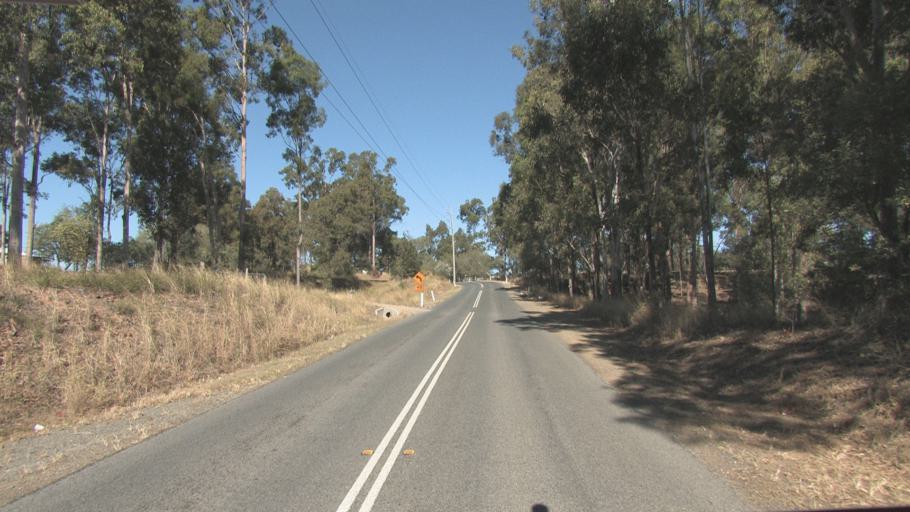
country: AU
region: Queensland
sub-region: Logan
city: Cedar Vale
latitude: -27.8802
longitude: 153.0157
